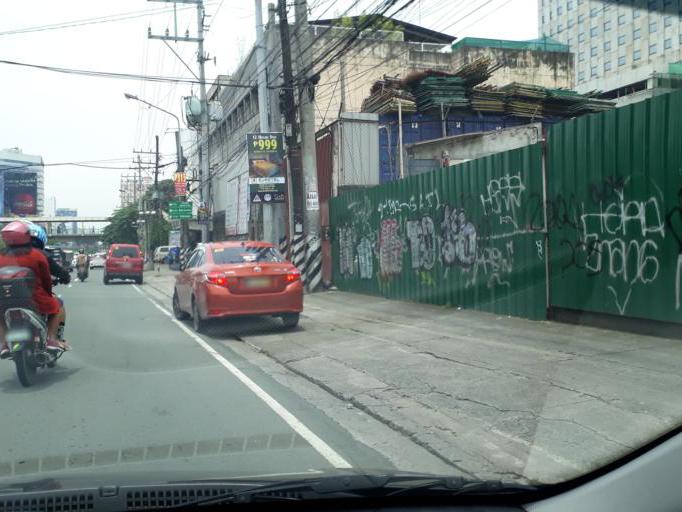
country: PH
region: Calabarzon
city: Bagong Pagasa
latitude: 14.6549
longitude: 121.0339
